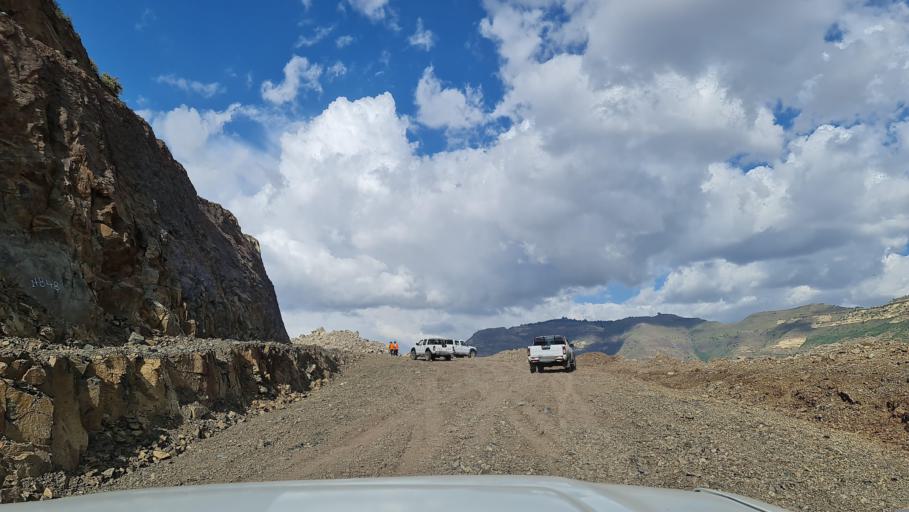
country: ET
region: Amhara
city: Debark'
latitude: 13.1188
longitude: 38.0219
